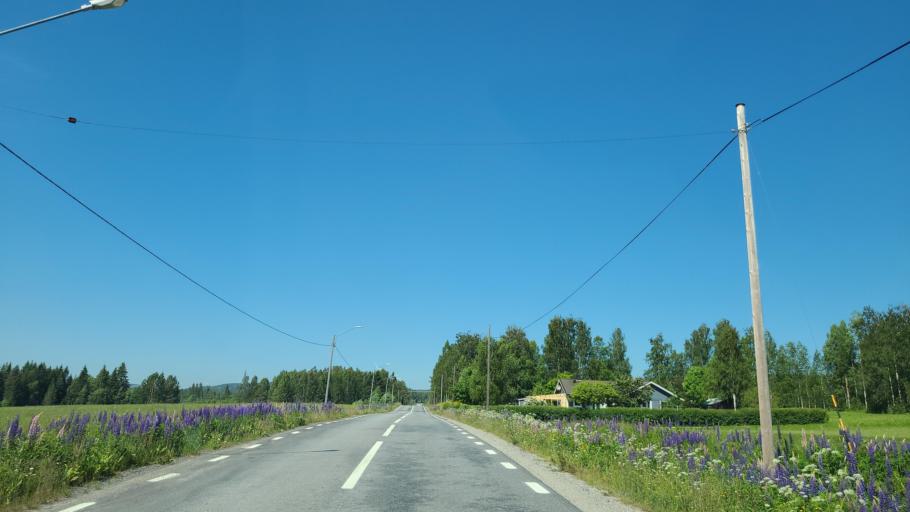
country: SE
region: Vaesternorrland
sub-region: OErnskoeldsviks Kommun
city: Husum
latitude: 63.5802
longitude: 19.0271
